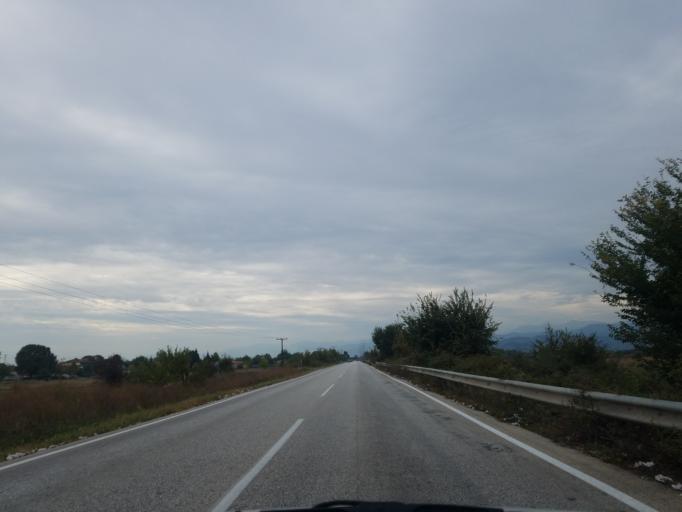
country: GR
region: Thessaly
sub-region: Nomos Kardhitsas
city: Agnantero
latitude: 39.4903
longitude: 21.8384
